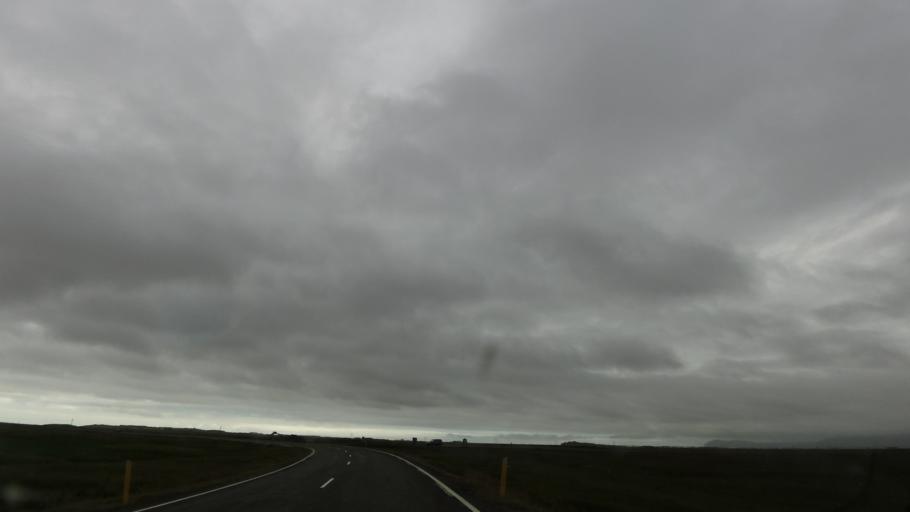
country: IS
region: East
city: Hoefn
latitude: 64.3177
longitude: -15.4137
